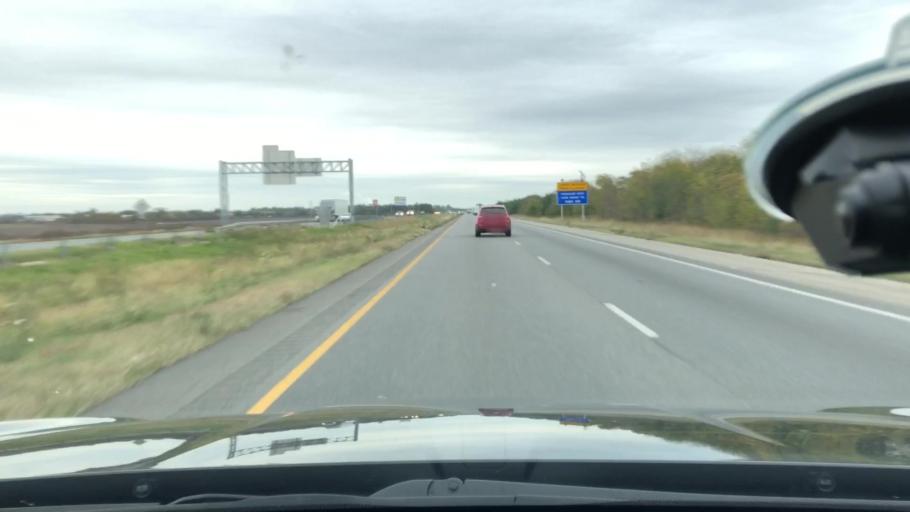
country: US
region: Arkansas
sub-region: Miller County
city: Texarkana
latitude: 33.5024
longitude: -93.9554
